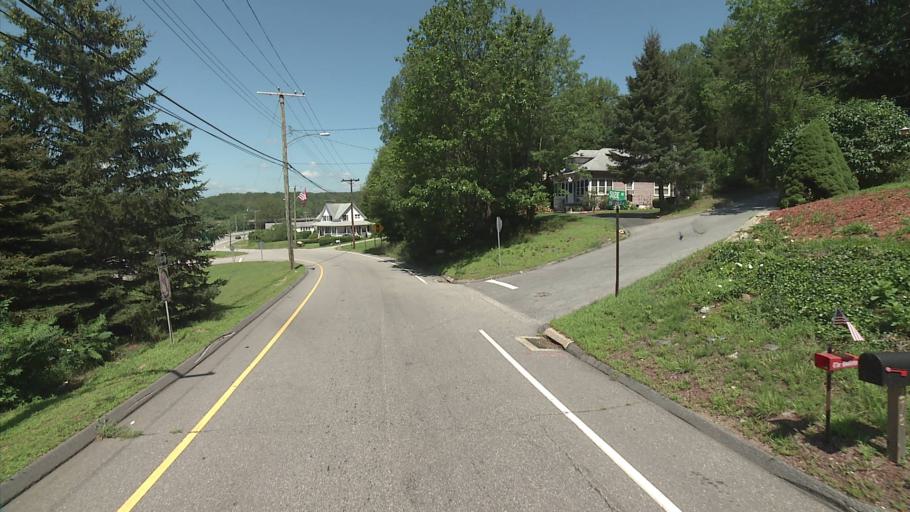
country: US
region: Connecticut
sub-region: Windham County
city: Moosup
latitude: 41.7158
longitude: -71.8913
